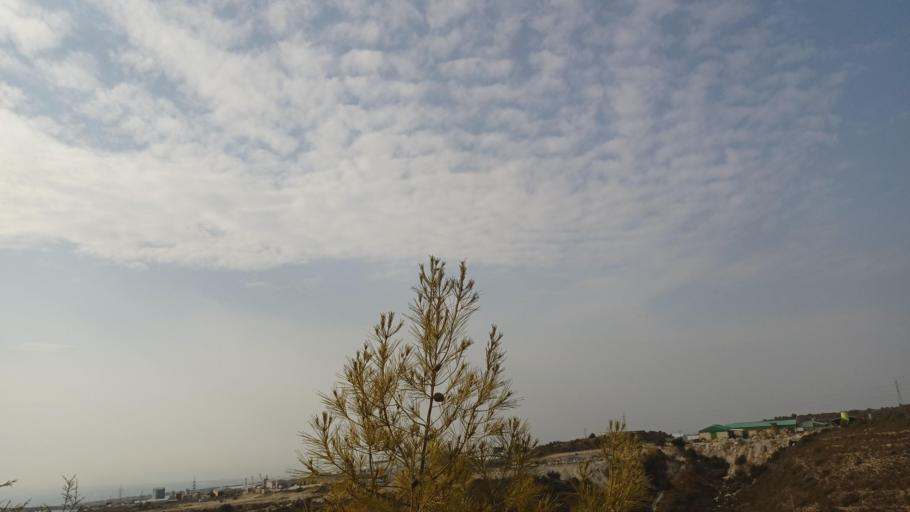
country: CY
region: Limassol
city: Ypsonas
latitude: 34.7429
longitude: 32.9474
